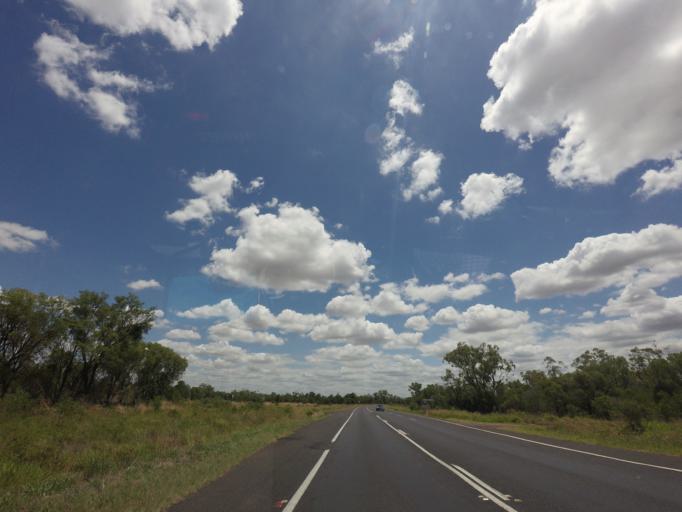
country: AU
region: New South Wales
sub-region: Moree Plains
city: Boggabilla
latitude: -28.7398
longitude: 150.2676
